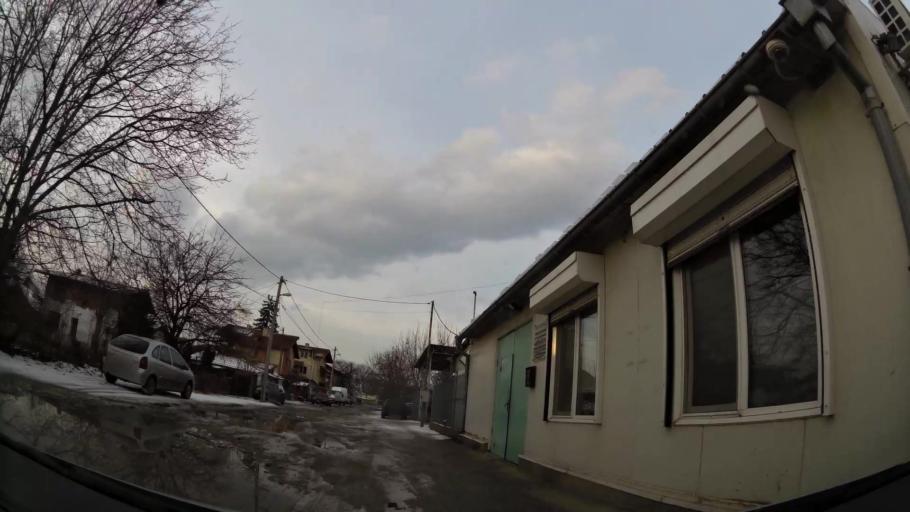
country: BG
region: Sofia-Capital
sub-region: Stolichna Obshtina
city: Sofia
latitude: 42.7221
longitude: 23.3480
